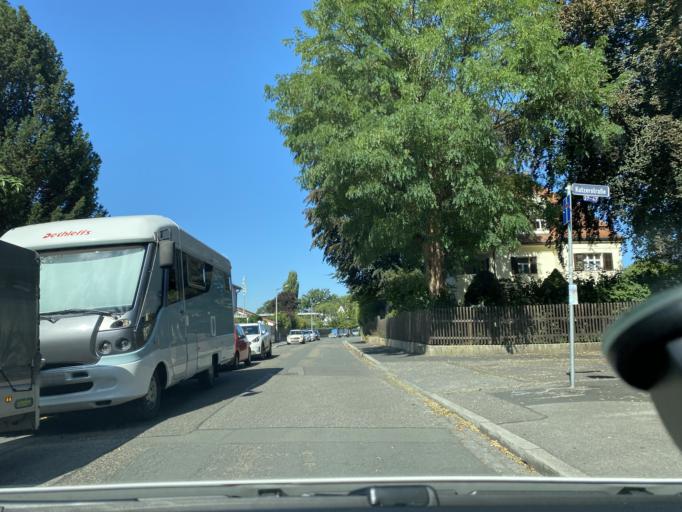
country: DE
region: Bavaria
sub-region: Regierungsbezirk Mittelfranken
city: Furth
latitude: 49.4761
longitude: 11.0046
